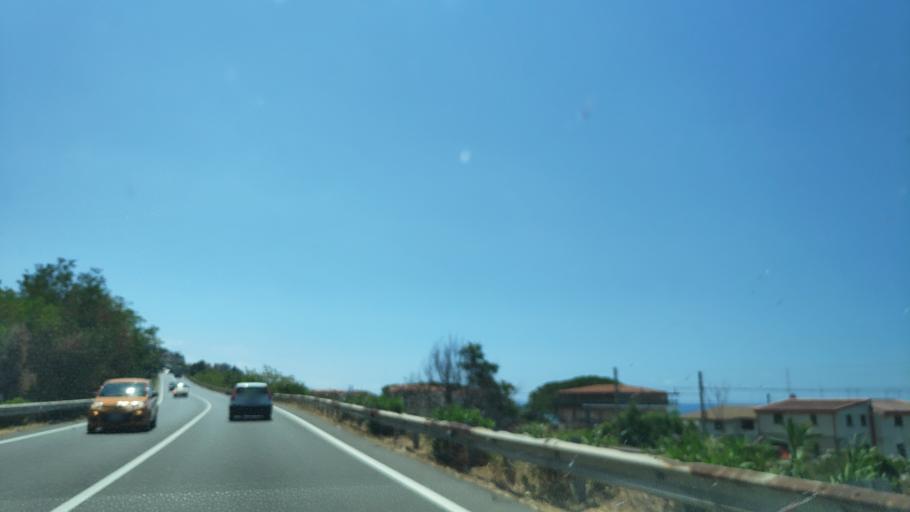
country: IT
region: Calabria
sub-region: Provincia di Cosenza
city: Acquappesa
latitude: 39.4845
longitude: 15.9578
